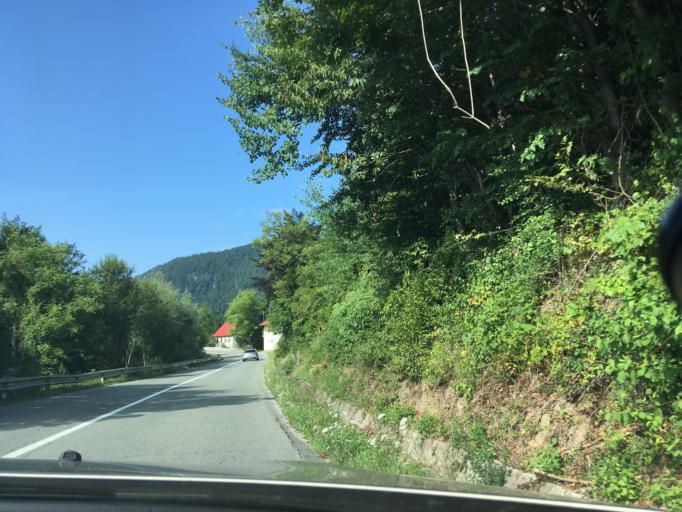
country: HR
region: Primorsko-Goranska
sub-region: Grad Delnice
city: Delnice
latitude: 45.4230
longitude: 14.8275
